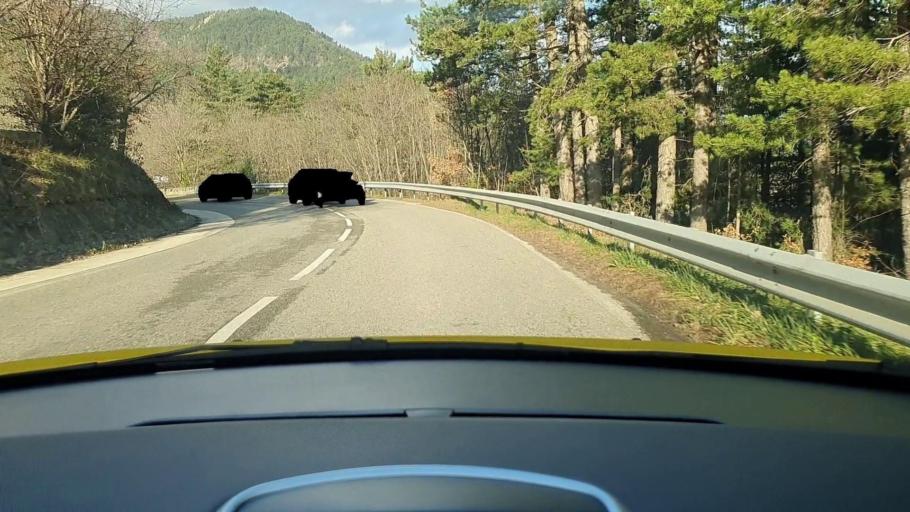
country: FR
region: Languedoc-Roussillon
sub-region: Departement du Gard
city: Branoux-les-Taillades
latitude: 44.3788
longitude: 3.9417
